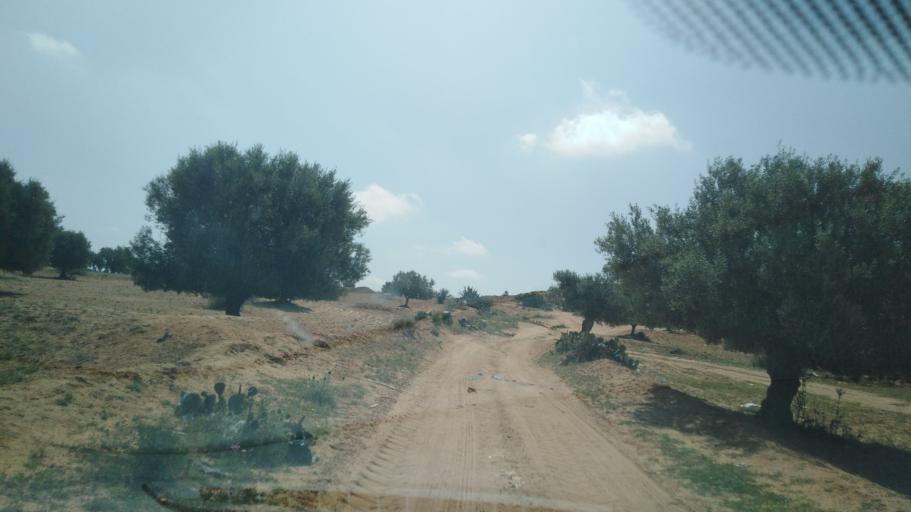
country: TN
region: Safaqis
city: Sfax
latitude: 34.7279
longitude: 10.5695
